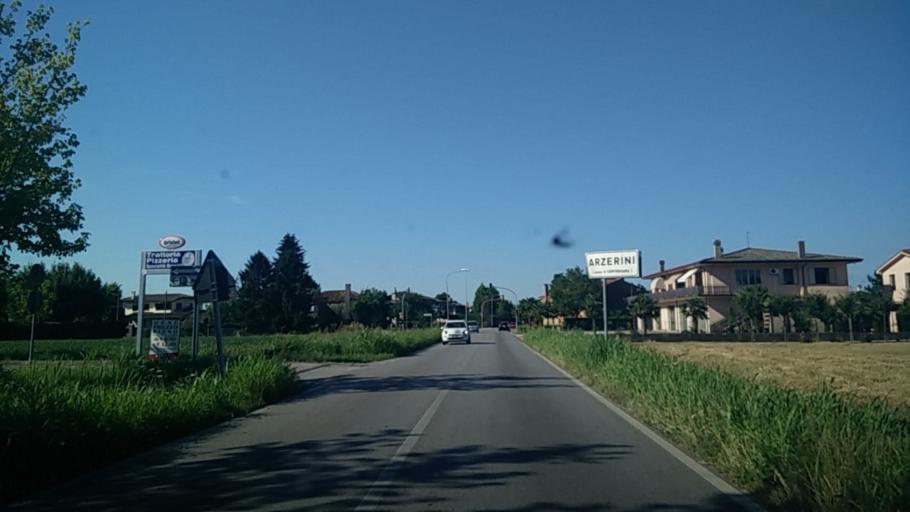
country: IT
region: Veneto
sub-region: Provincia di Venezia
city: Camponogara
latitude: 45.3987
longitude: 12.0820
